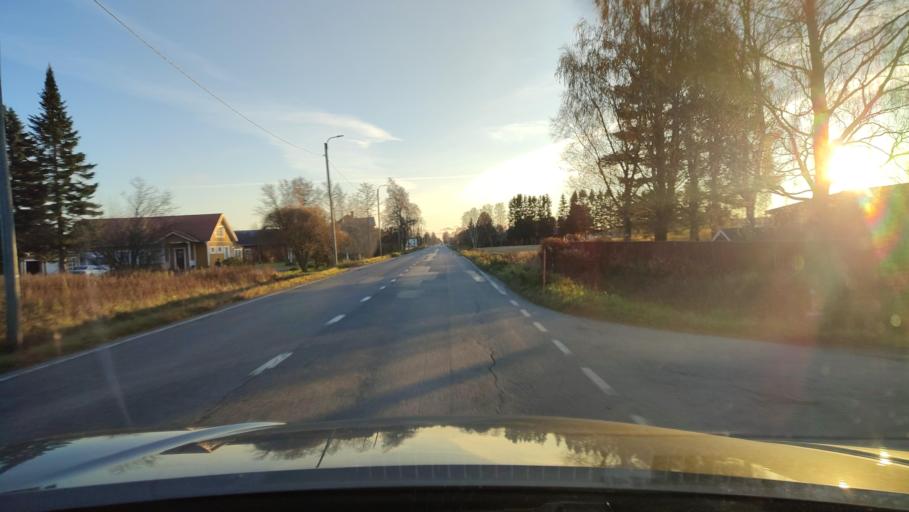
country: FI
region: Ostrobothnia
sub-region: Sydosterbotten
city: Naerpes
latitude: 62.5405
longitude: 21.3918
